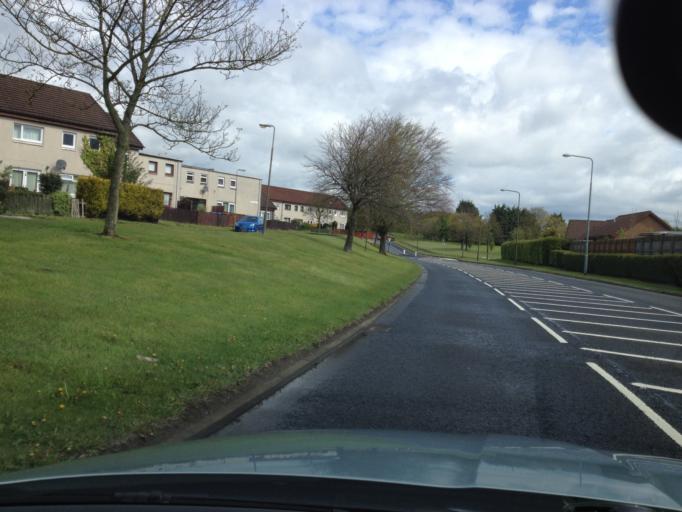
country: GB
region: Scotland
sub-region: West Lothian
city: Mid Calder
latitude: 55.8952
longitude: -3.4900
